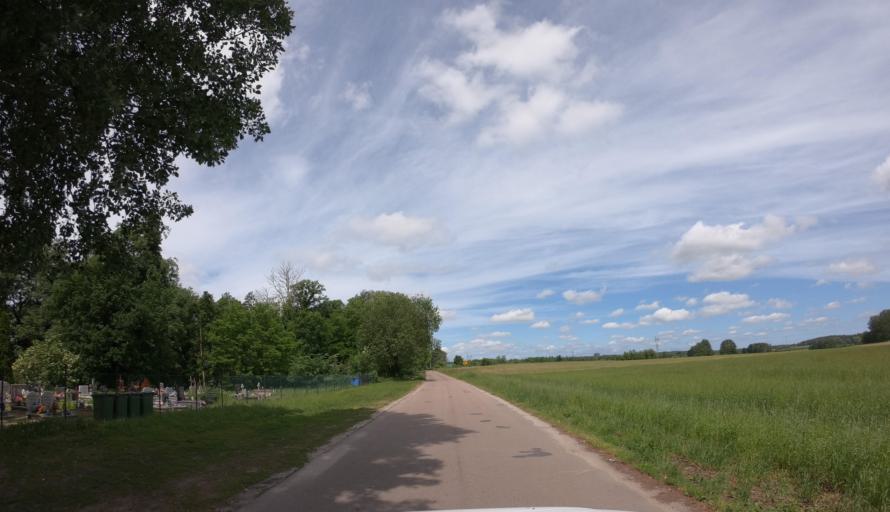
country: PL
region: West Pomeranian Voivodeship
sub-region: Powiat kamienski
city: Wolin
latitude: 53.8261
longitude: 14.7086
